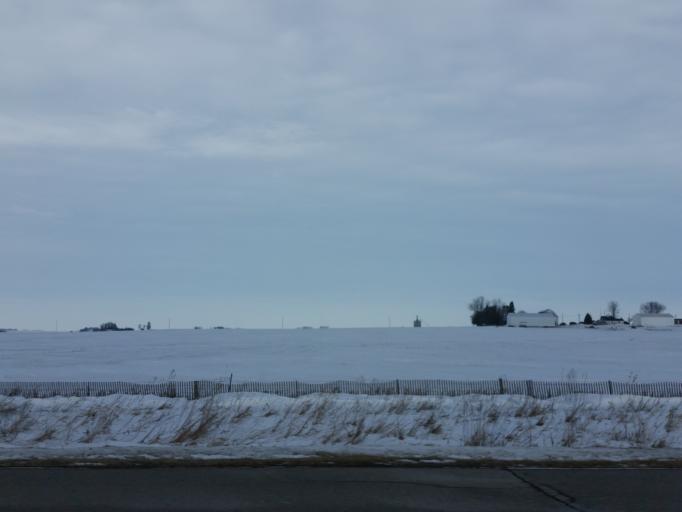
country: US
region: Iowa
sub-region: Delaware County
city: Manchester
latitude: 42.4645
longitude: -91.5927
